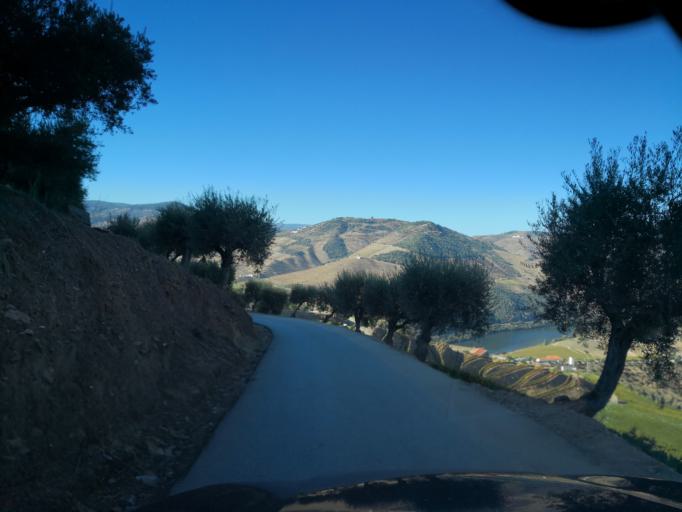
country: PT
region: Viseu
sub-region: Tabuaco
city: Tabuaco
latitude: 41.1720
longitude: -7.5139
